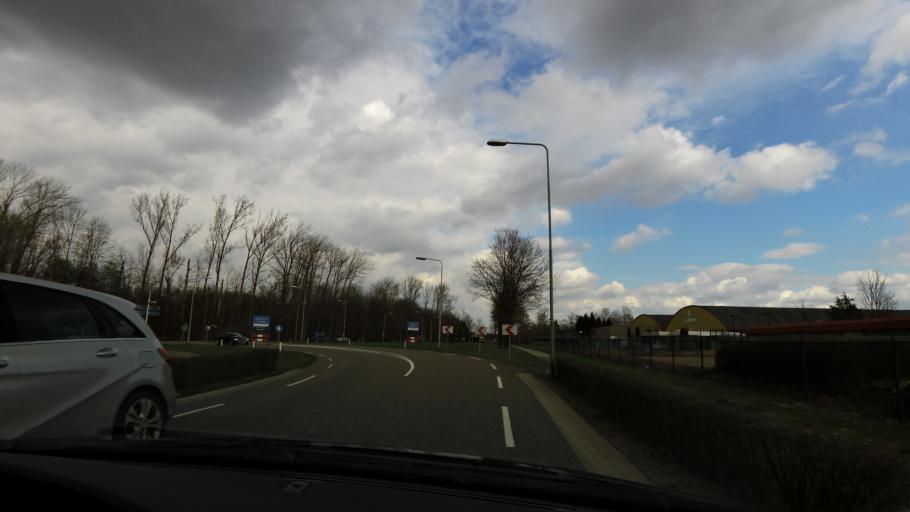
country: NL
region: Limburg
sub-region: Gemeente Sittard-Geleen
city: Limbricht
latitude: 51.0732
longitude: 5.8637
